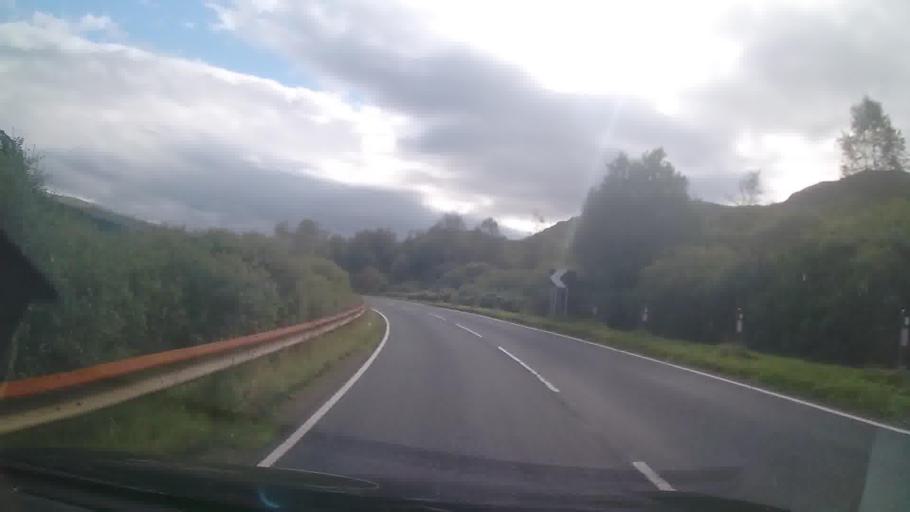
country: GB
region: Scotland
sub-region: Argyll and Bute
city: Garelochhead
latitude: 56.3127
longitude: -5.0850
